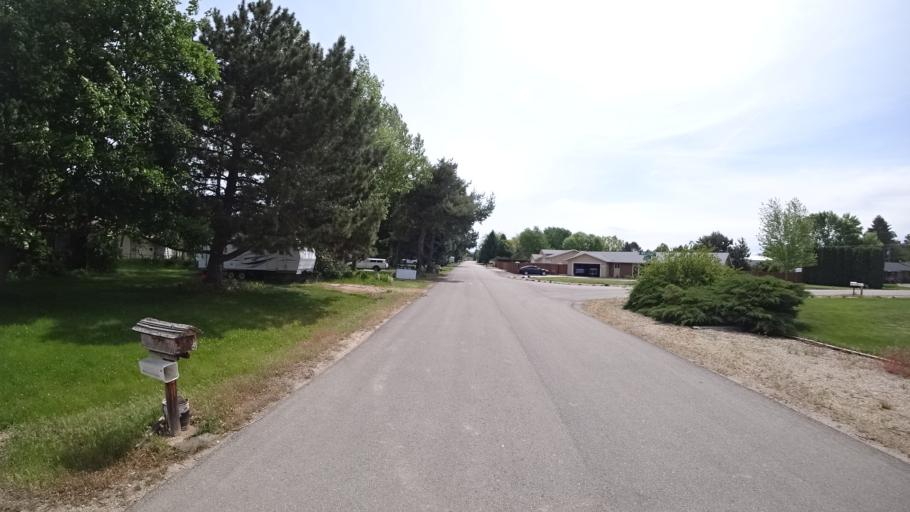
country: US
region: Idaho
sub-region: Ada County
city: Meridian
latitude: 43.5822
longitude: -116.3193
